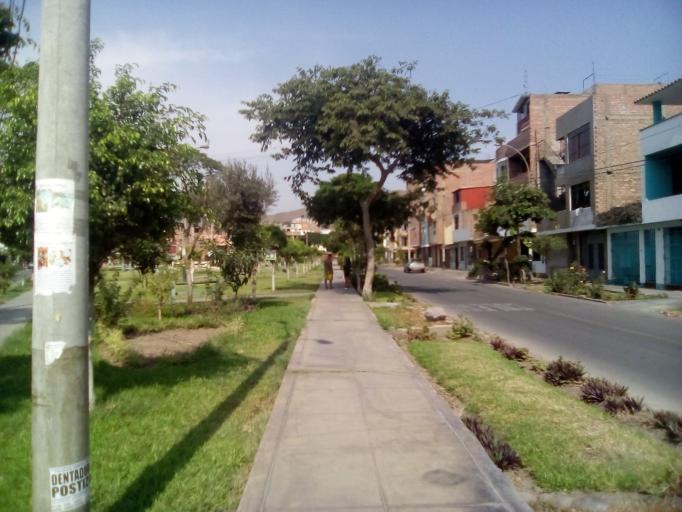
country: PE
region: Lima
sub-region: Lima
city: Independencia
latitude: -11.9965
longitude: -77.0822
